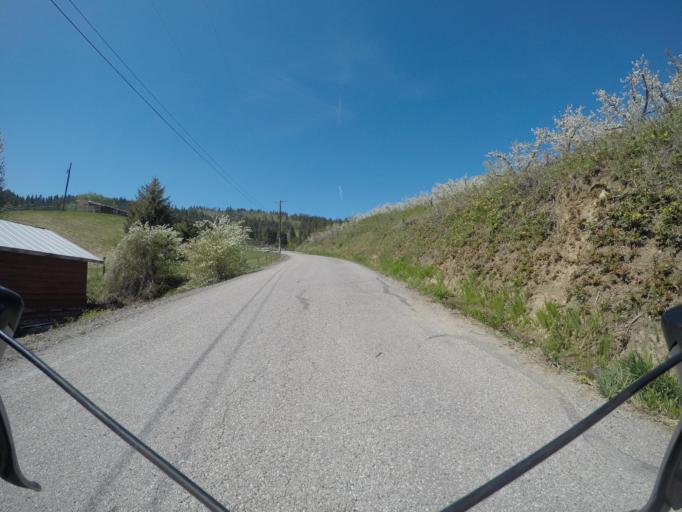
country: US
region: Washington
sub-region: Chelan County
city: Cashmere
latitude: 47.5398
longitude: -120.5724
